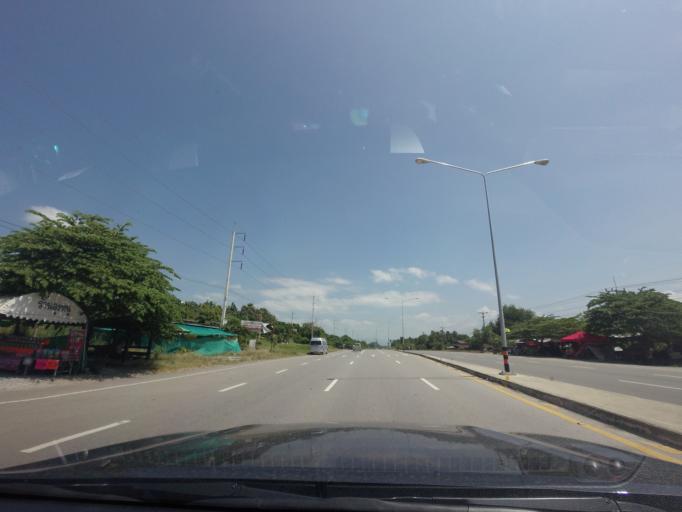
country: TH
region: Phetchabun
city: Lom Sak
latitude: 16.7656
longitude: 101.1554
